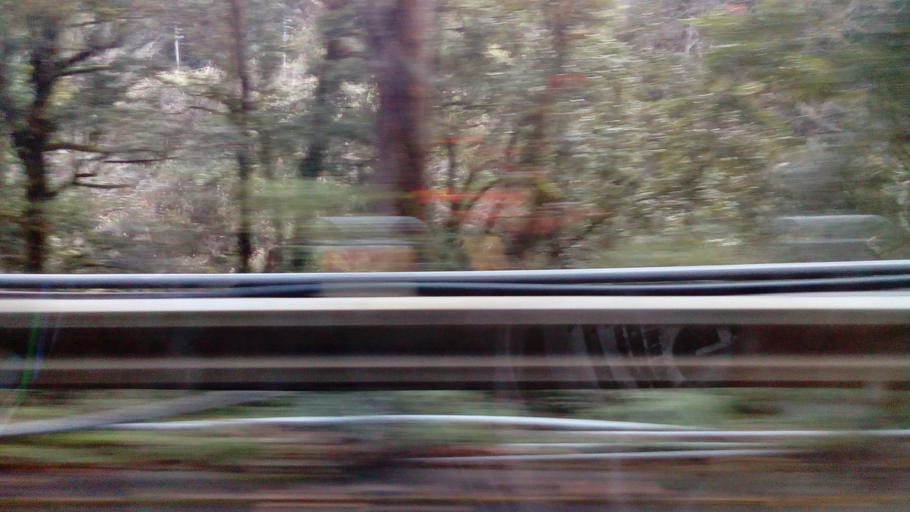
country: TW
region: Taiwan
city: Daxi
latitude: 24.4064
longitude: 121.3564
